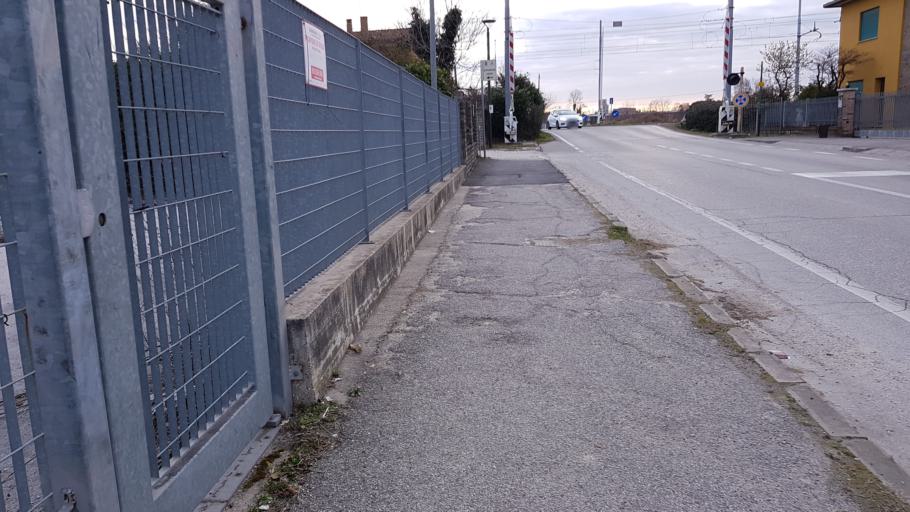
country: IT
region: Veneto
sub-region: Provincia di Padova
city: San Giorgio delle Pertiche
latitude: 45.5413
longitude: 11.9162
